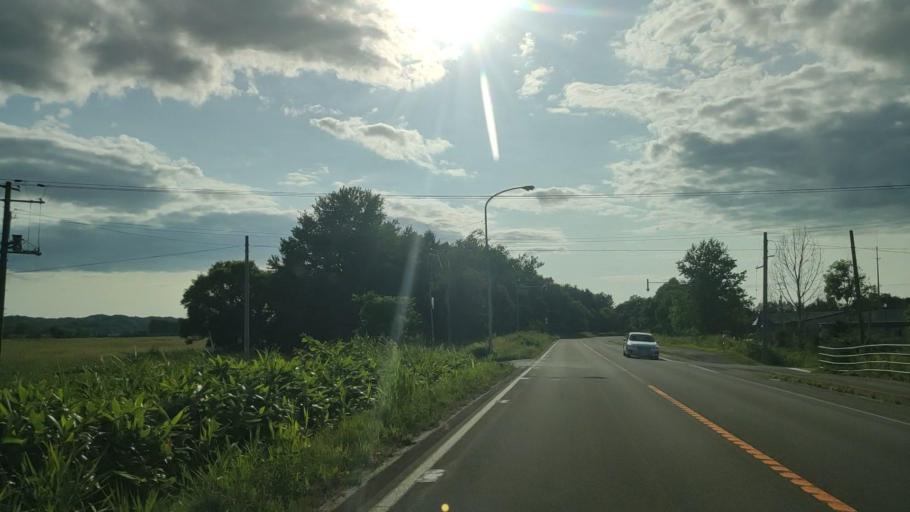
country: JP
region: Hokkaido
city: Makubetsu
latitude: 44.8969
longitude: 141.9205
